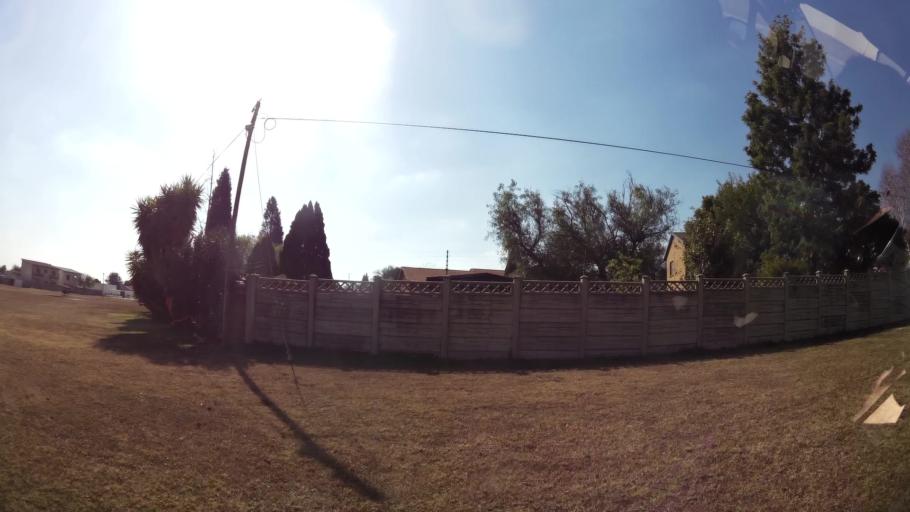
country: ZA
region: Gauteng
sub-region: West Rand District Municipality
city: Randfontein
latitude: -26.1514
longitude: 27.6914
